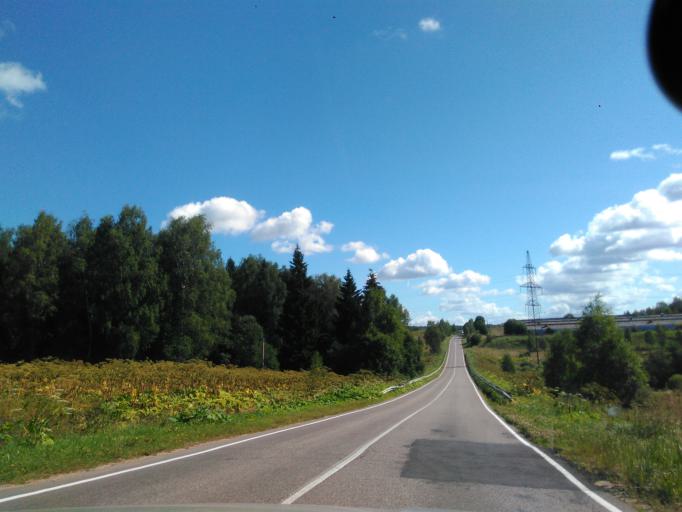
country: RU
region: Moskovskaya
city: Klin
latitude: 56.1805
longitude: 36.7951
